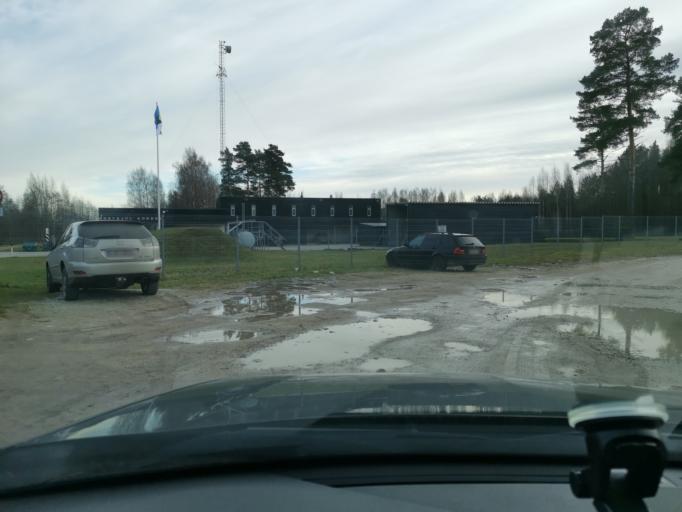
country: EE
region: Ida-Virumaa
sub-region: Sillamaee linn
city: Sillamae
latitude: 59.2581
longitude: 27.9150
